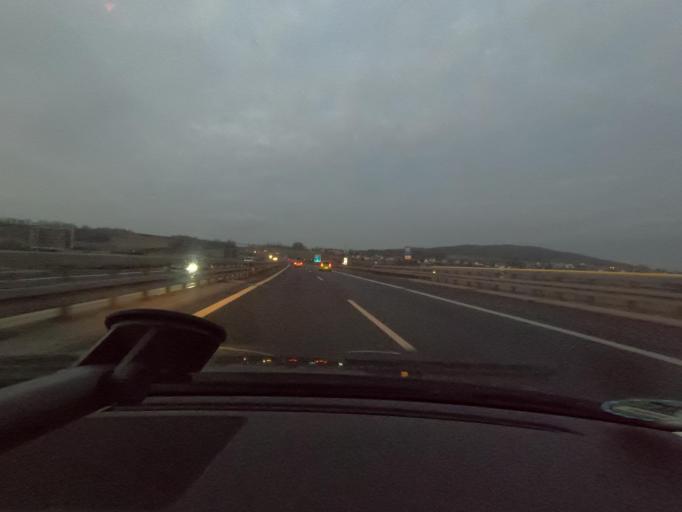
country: DE
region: Bavaria
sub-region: Upper Franconia
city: Lichtenfels
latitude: 50.1420
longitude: 11.0337
